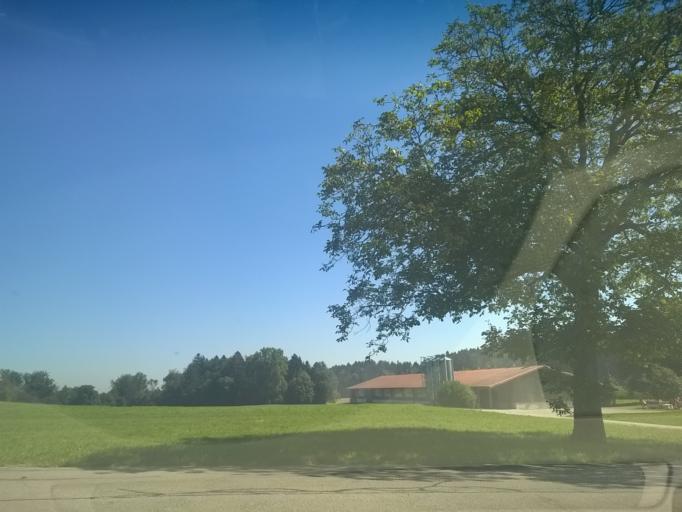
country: CH
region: Zurich
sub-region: Bezirk Winterthur
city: Brutten
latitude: 47.4841
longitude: 8.6580
